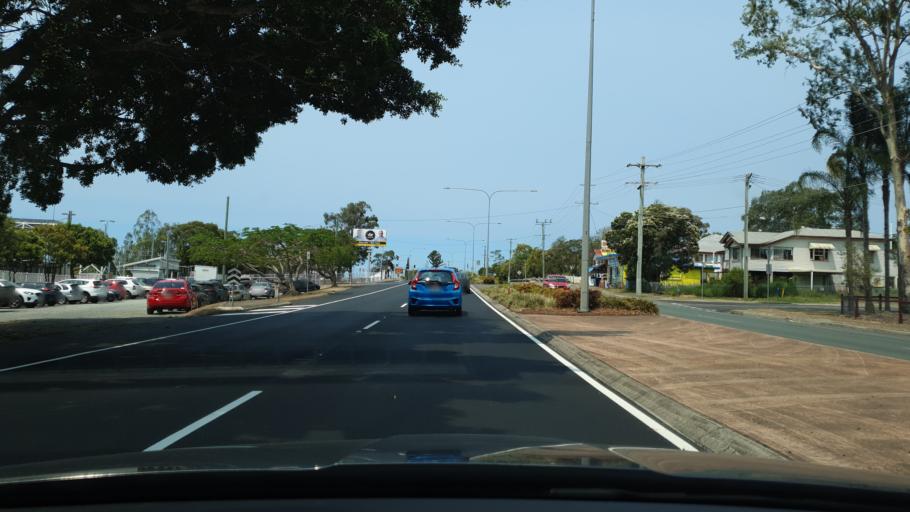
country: AU
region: Queensland
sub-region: Ipswich
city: Bundamba
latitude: -27.6040
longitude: 152.8214
